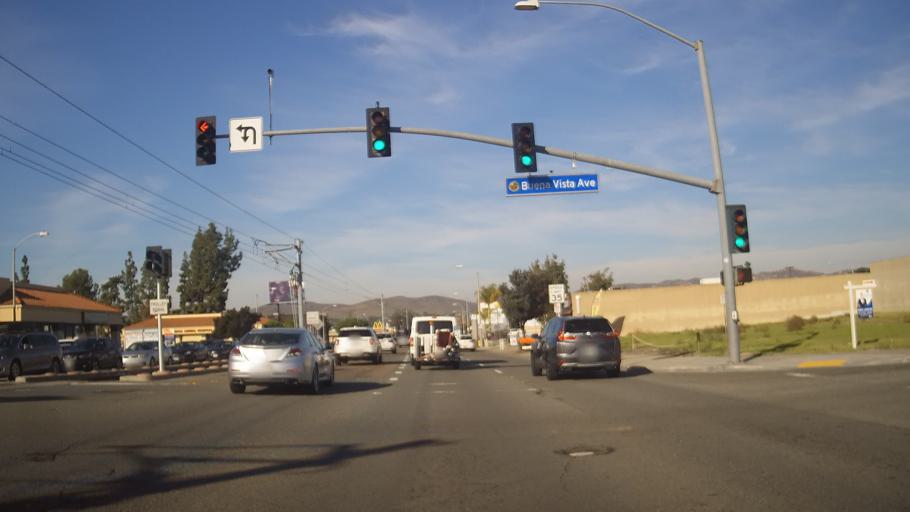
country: US
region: California
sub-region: San Diego County
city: Santee
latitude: 32.8350
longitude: -116.9837
